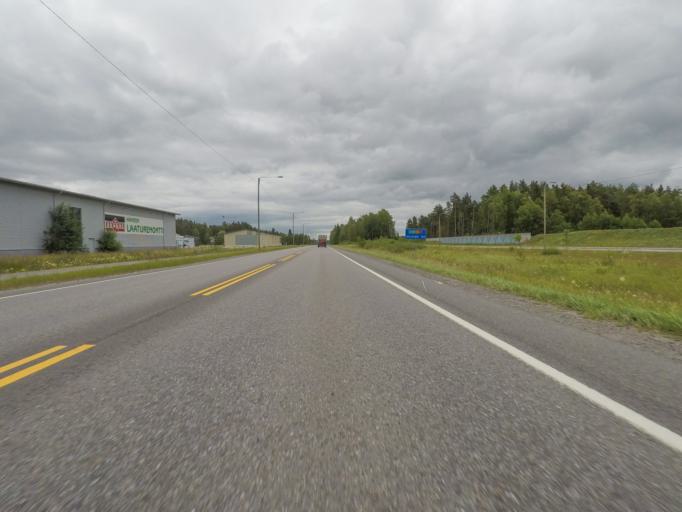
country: FI
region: Varsinais-Suomi
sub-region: Turku
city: Lieto
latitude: 60.4615
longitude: 22.4252
